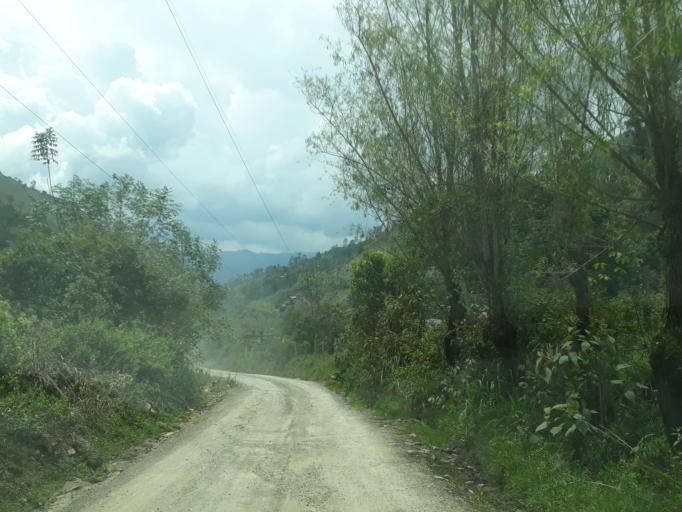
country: CO
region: Cundinamarca
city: Macheta
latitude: 5.0767
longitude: -73.5804
